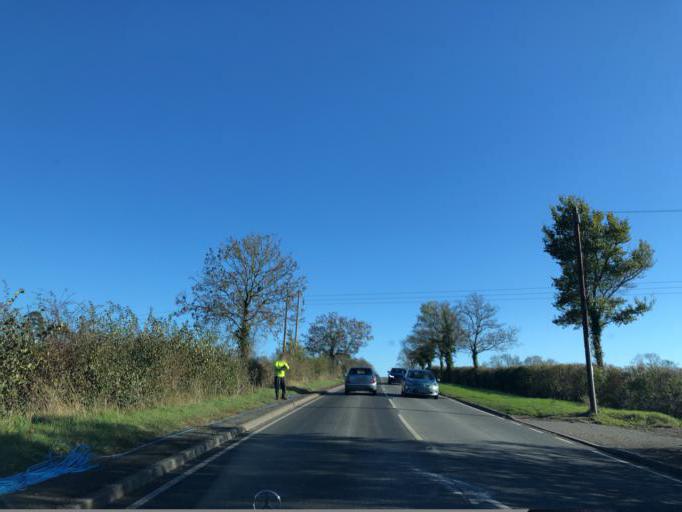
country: GB
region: England
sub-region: Warwickshire
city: Southam
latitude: 52.2498
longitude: -1.4066
